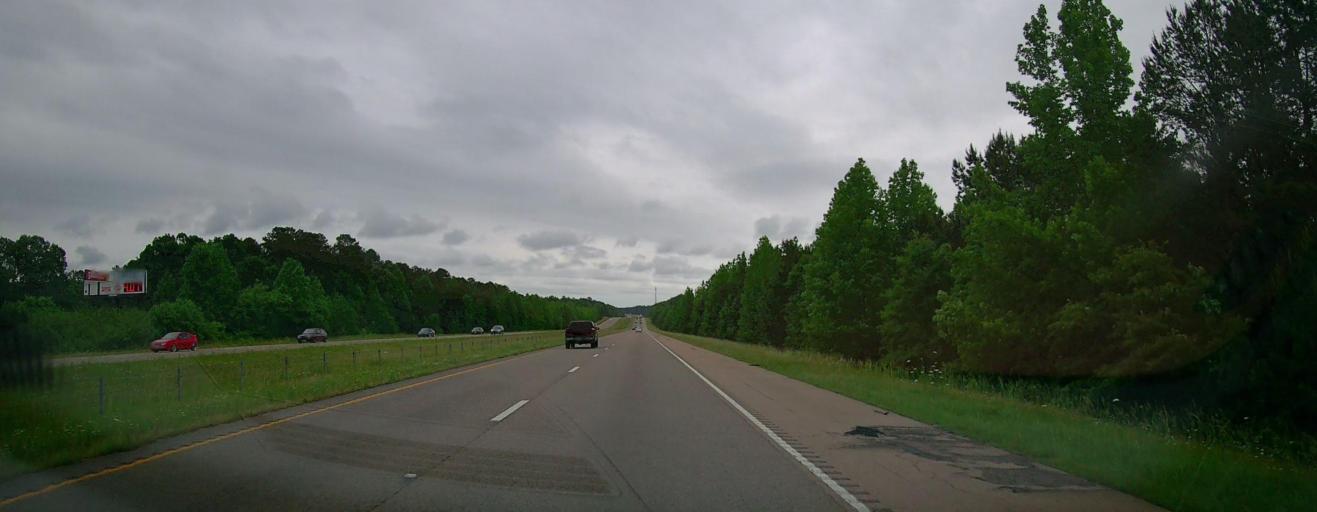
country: US
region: Mississippi
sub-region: Union County
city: New Albany
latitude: 34.5807
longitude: -89.1626
